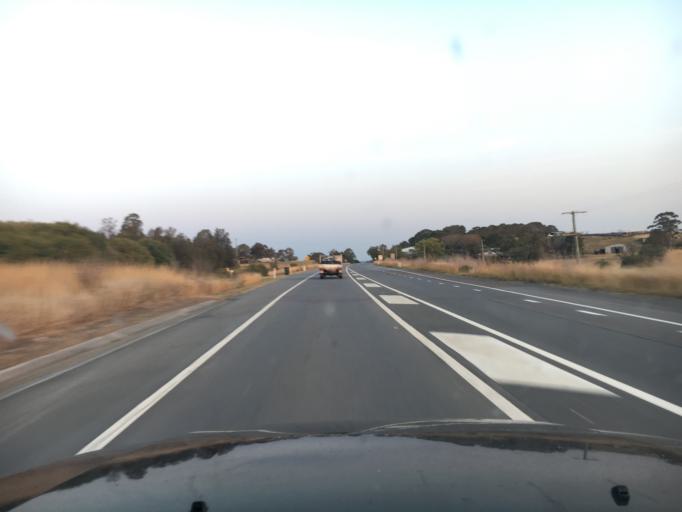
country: AU
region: New South Wales
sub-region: Cessnock
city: Greta
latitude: -32.7006
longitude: 151.4127
